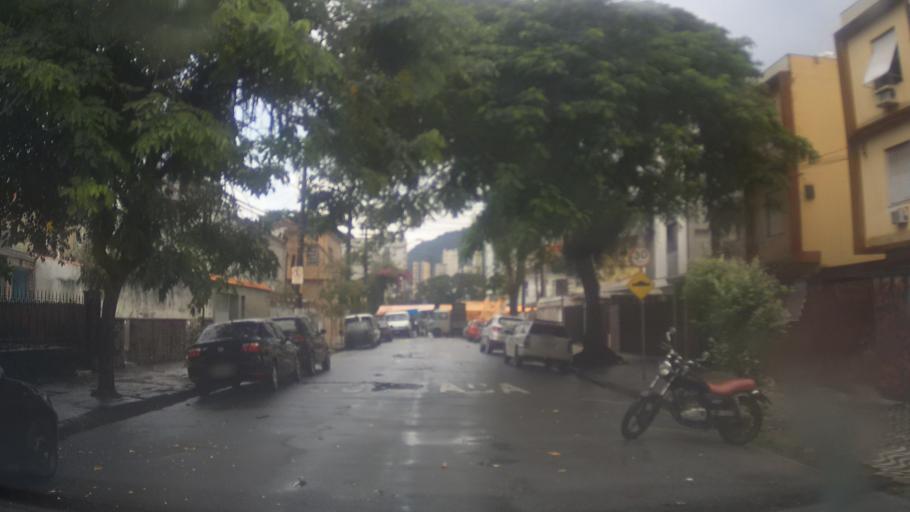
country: BR
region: Sao Paulo
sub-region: Santos
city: Santos
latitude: -23.9518
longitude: -46.3408
